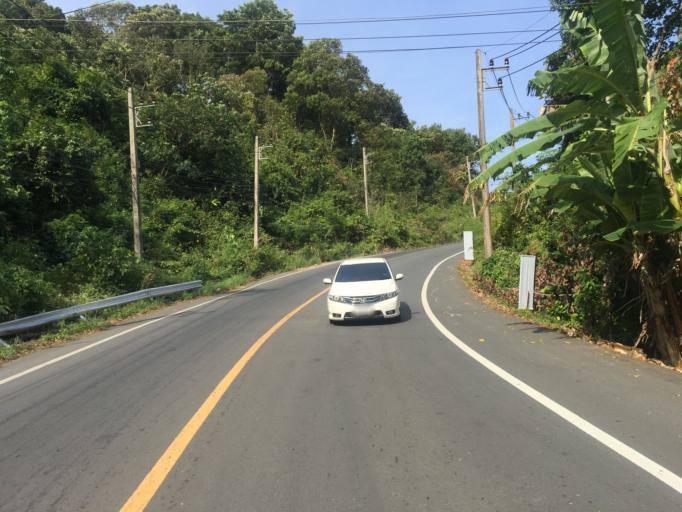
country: TH
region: Trat
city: Laem Ngop
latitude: 12.1410
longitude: 102.2778
